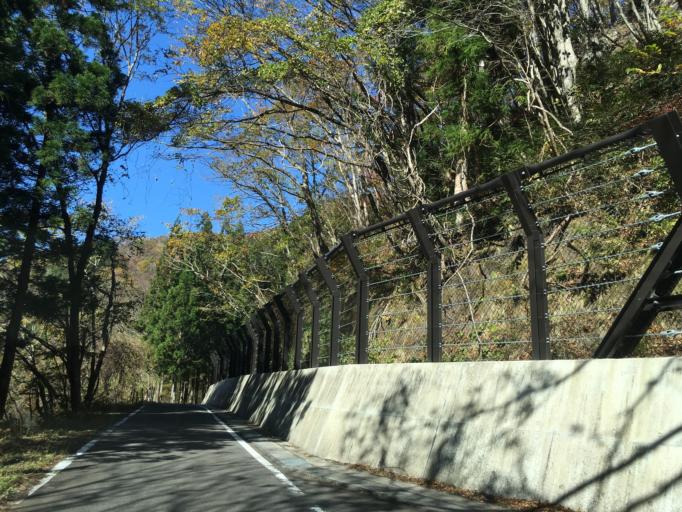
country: JP
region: Fukushima
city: Inawashiro
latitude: 37.3997
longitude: 140.0119
